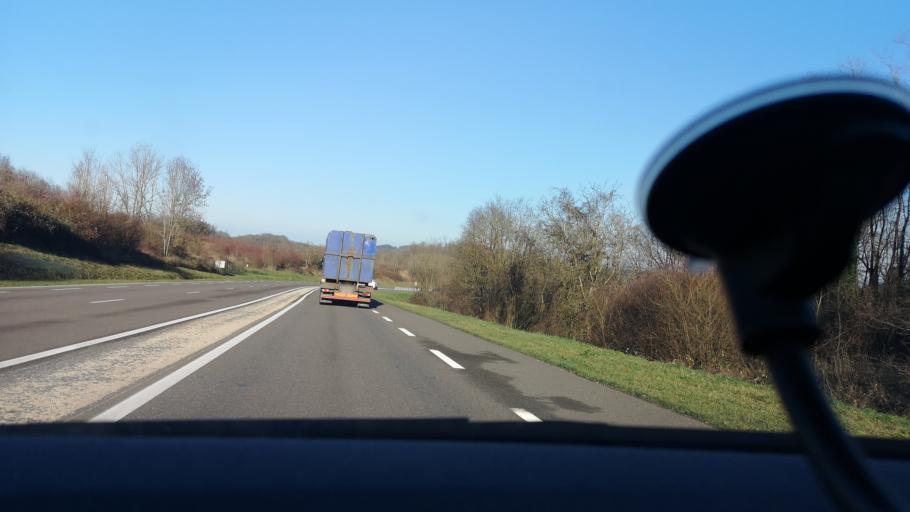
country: FR
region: Franche-Comte
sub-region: Departement du Jura
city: Bletterans
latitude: 46.7972
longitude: 5.5709
